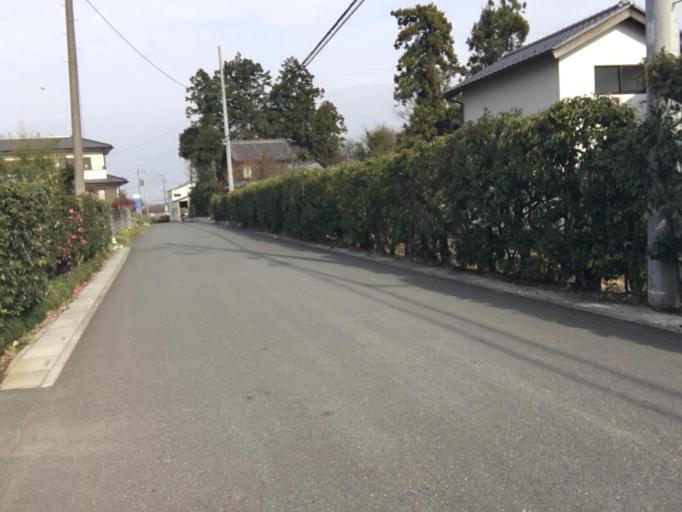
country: JP
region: Saitama
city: Yorii
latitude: 36.1397
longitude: 139.1999
